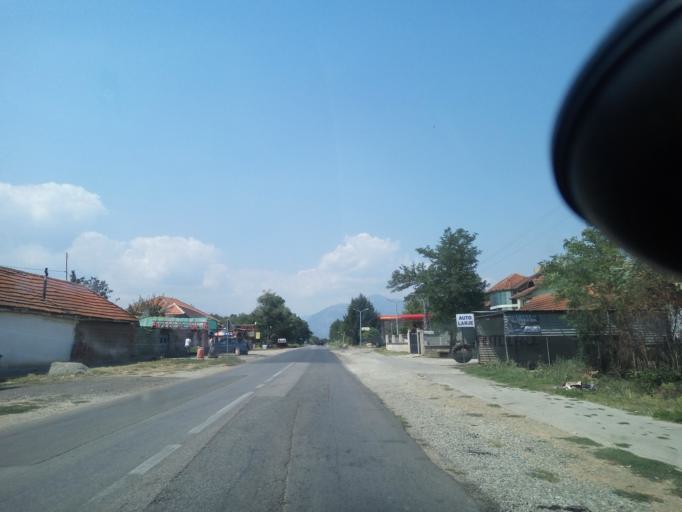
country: XK
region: Gjakova
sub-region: Komuna e Decanit
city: Gllogjan
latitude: 42.4596
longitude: 20.3520
